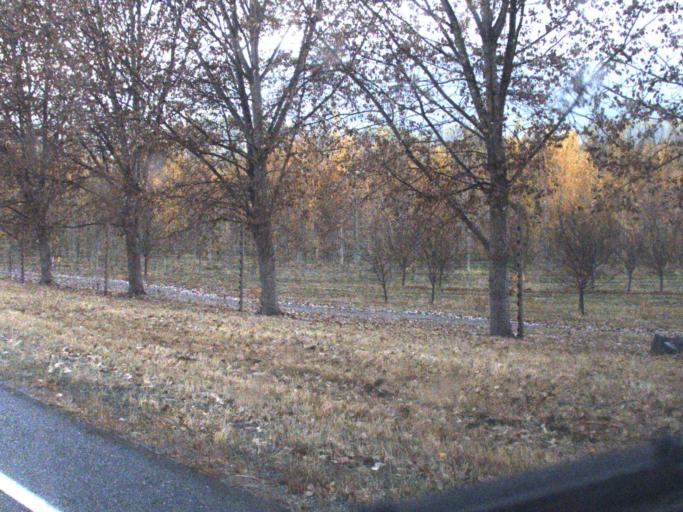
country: US
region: Washington
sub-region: Stevens County
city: Kettle Falls
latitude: 48.4696
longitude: -118.1731
